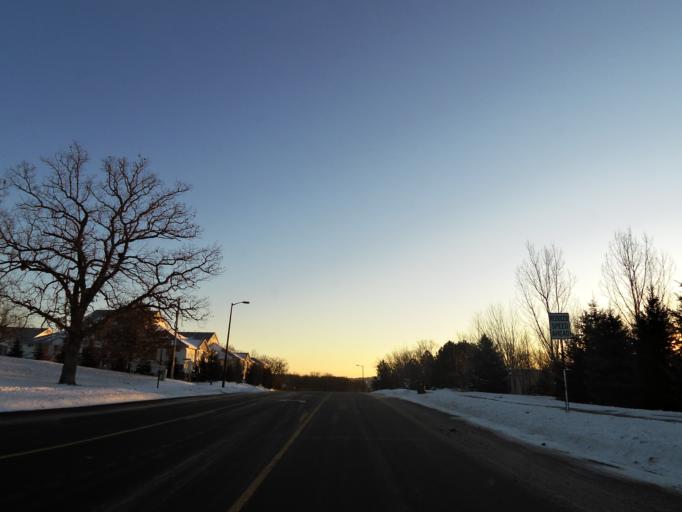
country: US
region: Minnesota
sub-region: Scott County
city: Prior Lake
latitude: 44.7319
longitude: -93.3730
